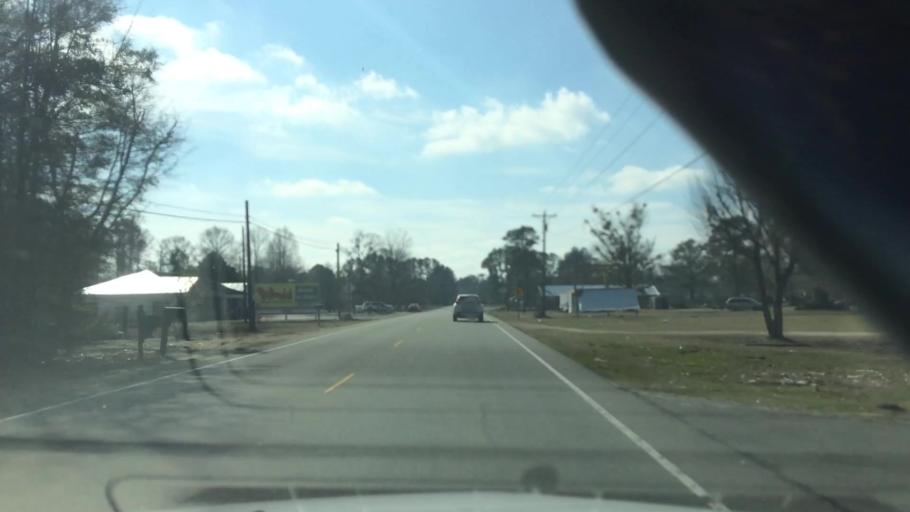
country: US
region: North Carolina
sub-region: Duplin County
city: Wallace
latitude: 34.7809
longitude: -77.9105
